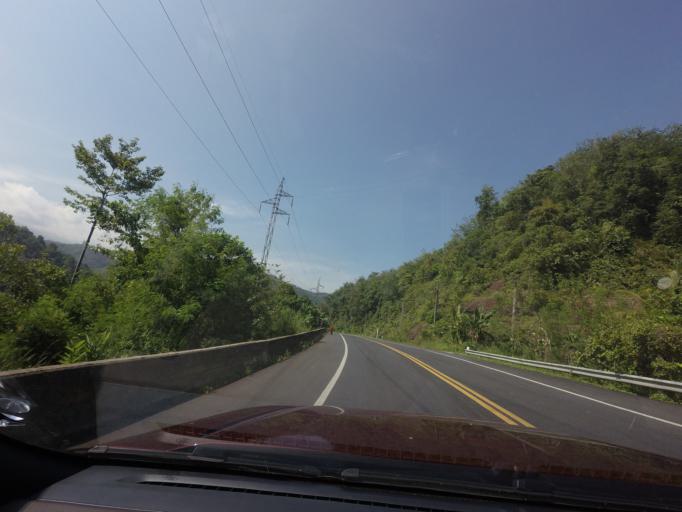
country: TH
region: Yala
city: Than To
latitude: 5.9787
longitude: 101.1999
